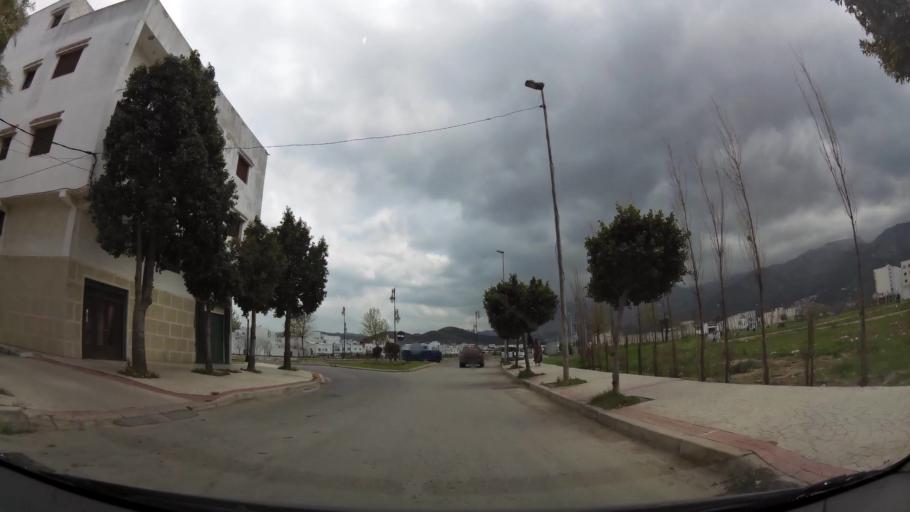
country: MA
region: Tanger-Tetouan
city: Tetouan
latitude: 35.5688
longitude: -5.3515
